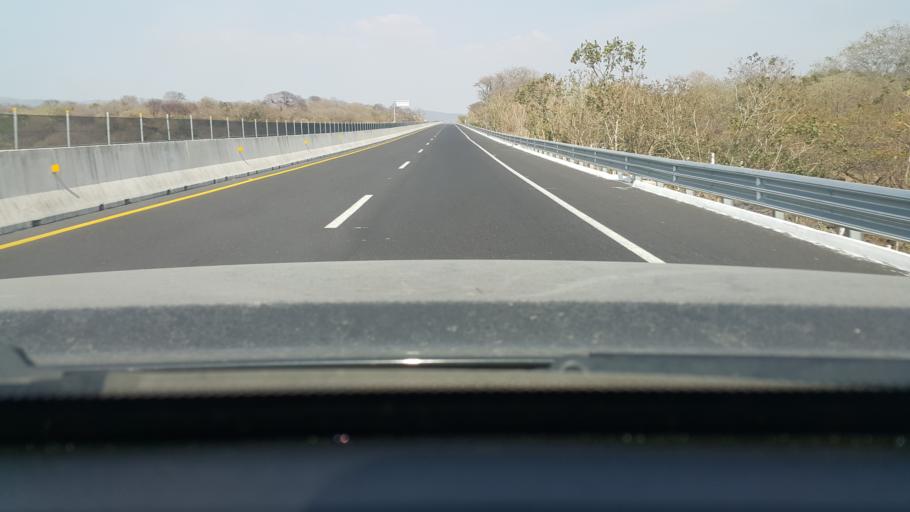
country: MX
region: Nayarit
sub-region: Ahuacatlan
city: Ahuacatlan
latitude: 21.0667
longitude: -104.4748
